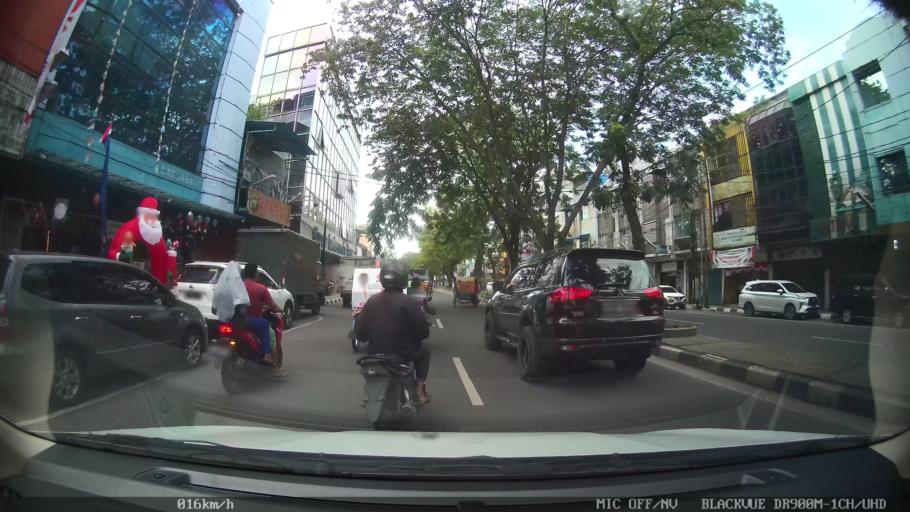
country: ID
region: North Sumatra
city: Medan
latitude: 3.5774
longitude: 98.6844
